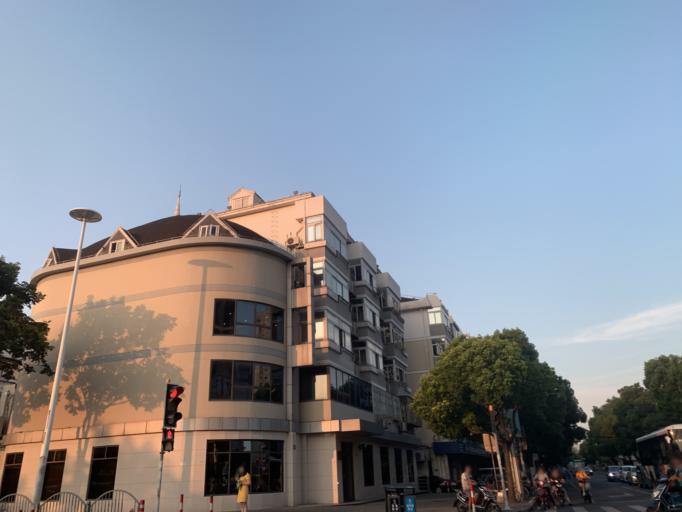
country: CN
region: Shanghai Shi
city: Huamu
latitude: 31.1854
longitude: 121.5504
